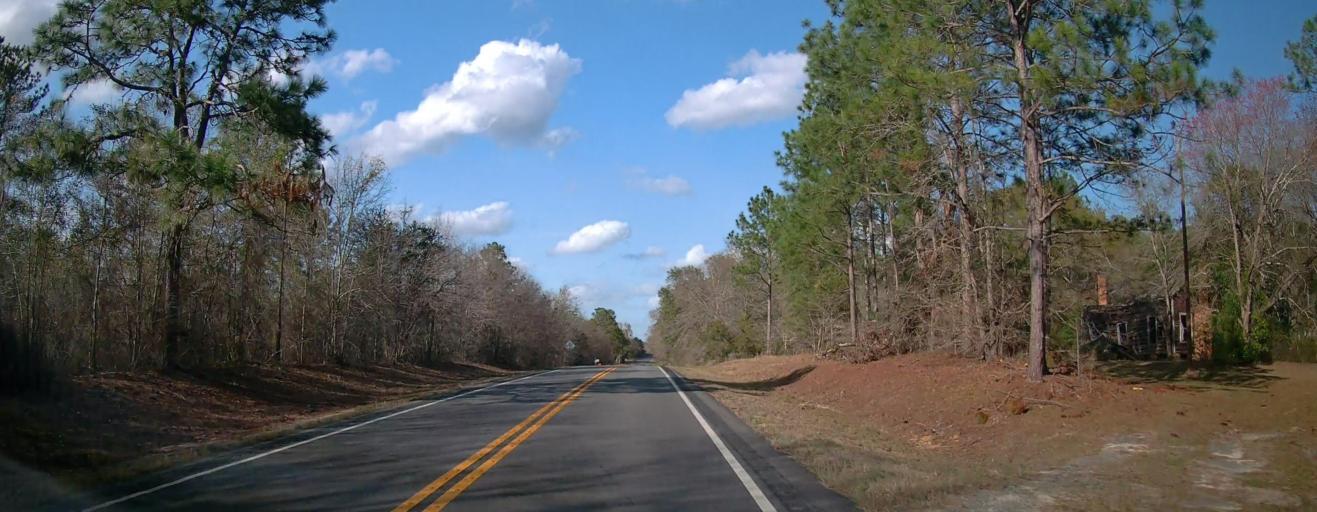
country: US
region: Georgia
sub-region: Wheeler County
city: Alamo
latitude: 32.0887
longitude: -82.8121
